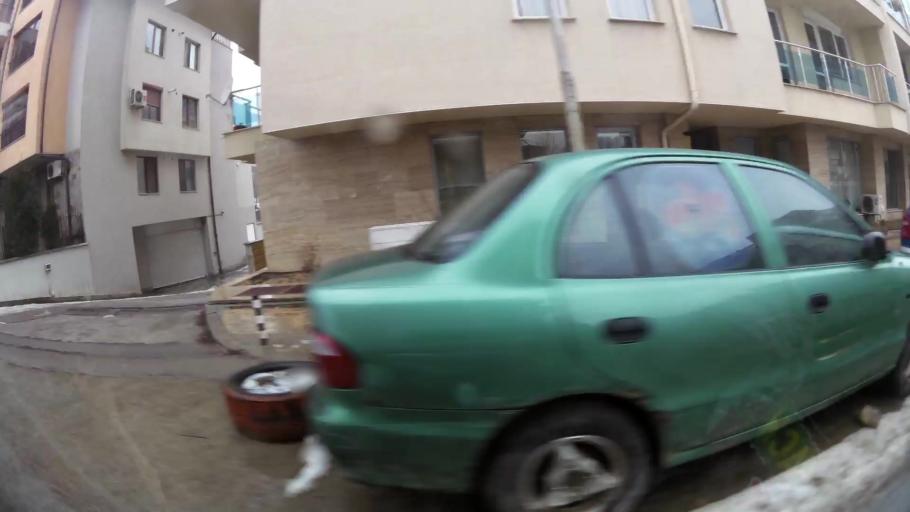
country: BG
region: Sofia-Capital
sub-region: Stolichna Obshtina
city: Sofia
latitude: 42.6566
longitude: 23.3010
